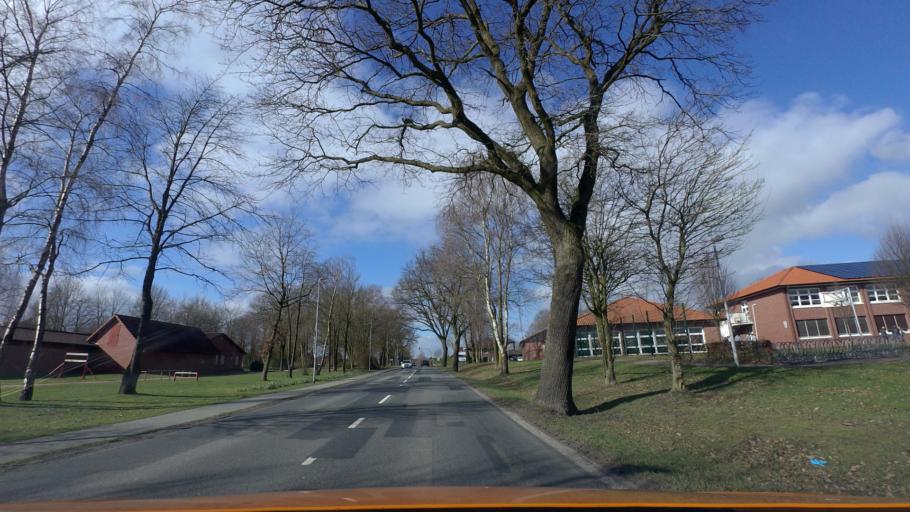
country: DE
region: Lower Saxony
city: Bosel
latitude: 53.0053
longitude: 7.9609
